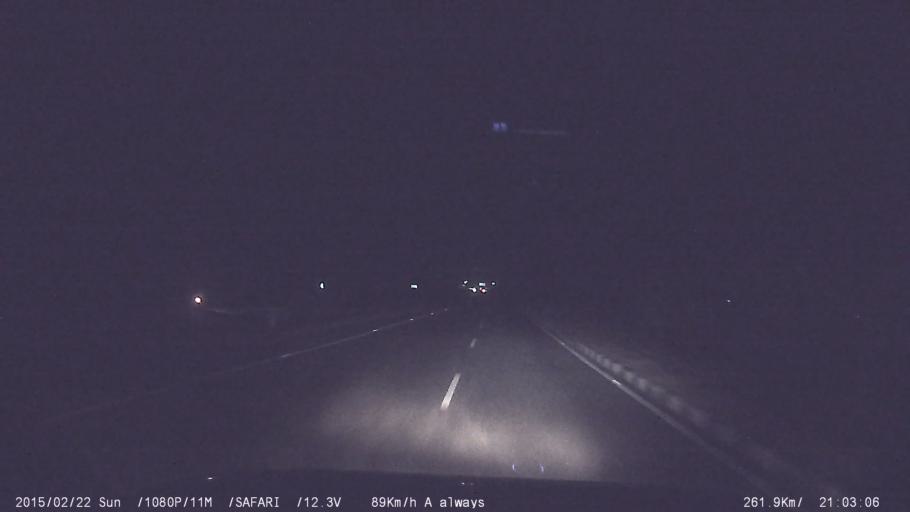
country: IN
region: Tamil Nadu
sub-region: Karur
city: Pallappatti
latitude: 10.6871
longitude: 77.9272
